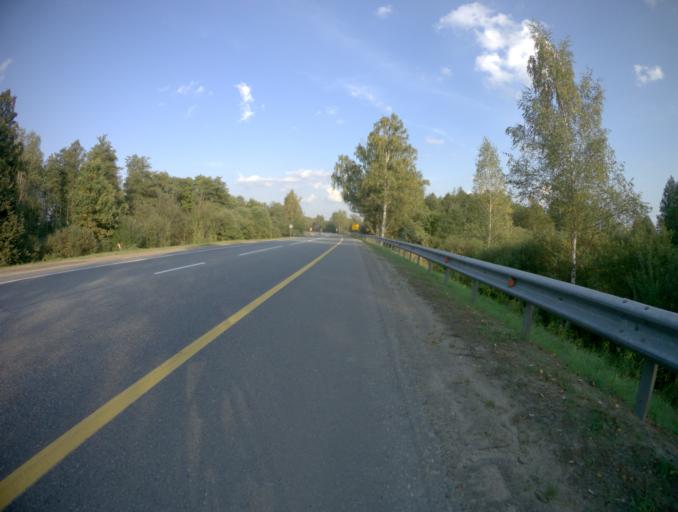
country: RU
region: Vladimir
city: Kameshkovo
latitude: 56.1956
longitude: 40.8847
